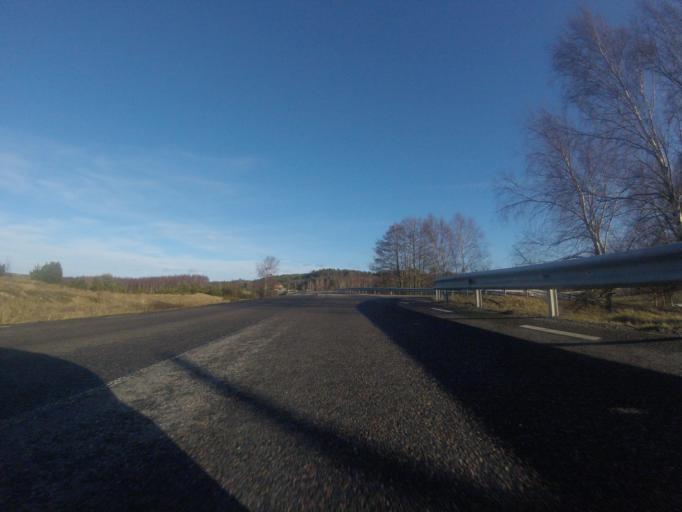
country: SE
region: Halland
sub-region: Varbergs Kommun
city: Veddige
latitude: 57.2196
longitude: 12.2348
